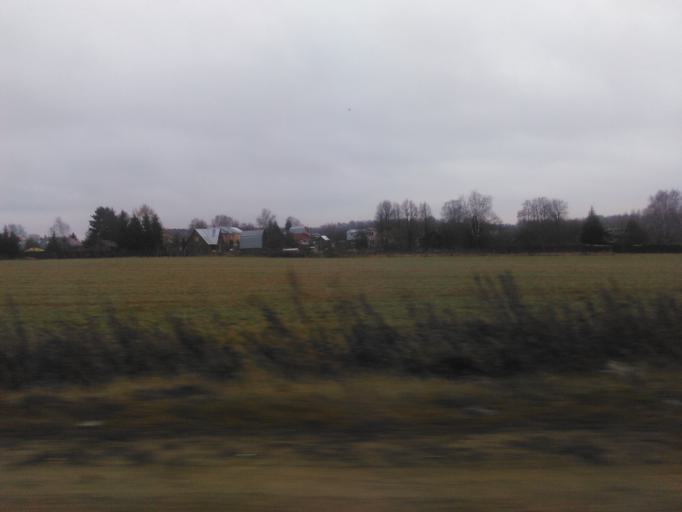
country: RU
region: Moskovskaya
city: Ashukino
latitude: 56.1556
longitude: 37.9675
